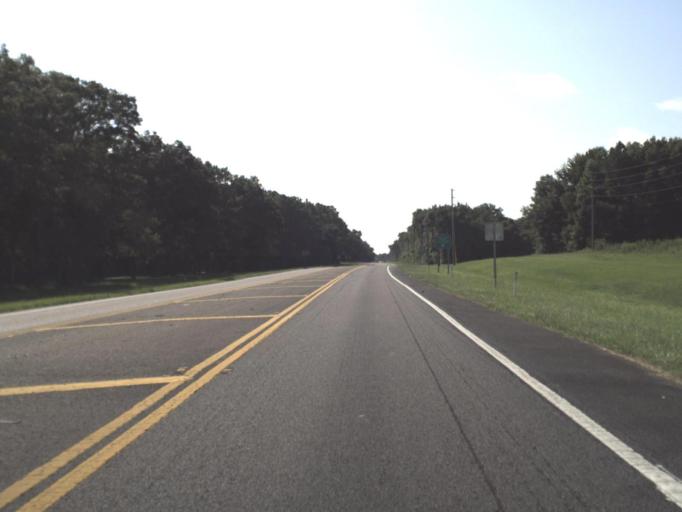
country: US
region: Florida
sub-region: Citrus County
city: Sugarmill Woods
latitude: 28.6753
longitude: -82.4827
